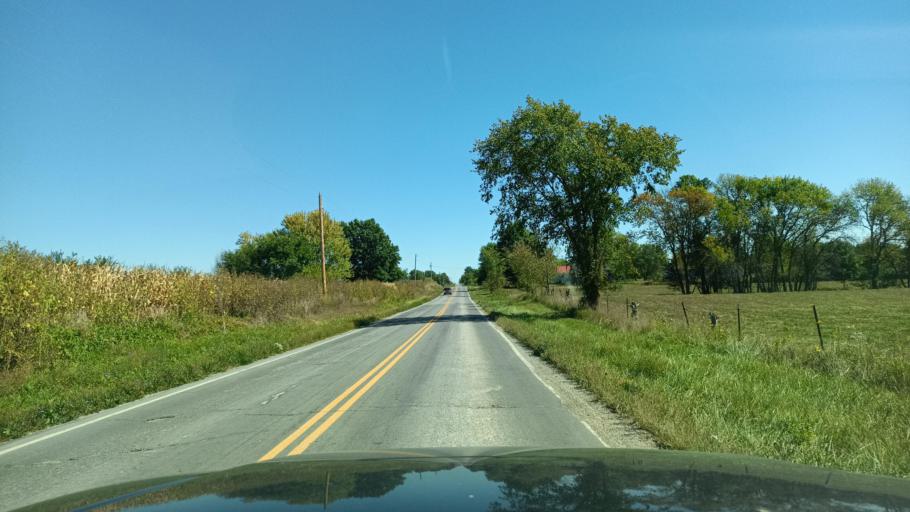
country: US
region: Missouri
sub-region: Macon County
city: La Plata
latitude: 40.0225
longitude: -92.5640
